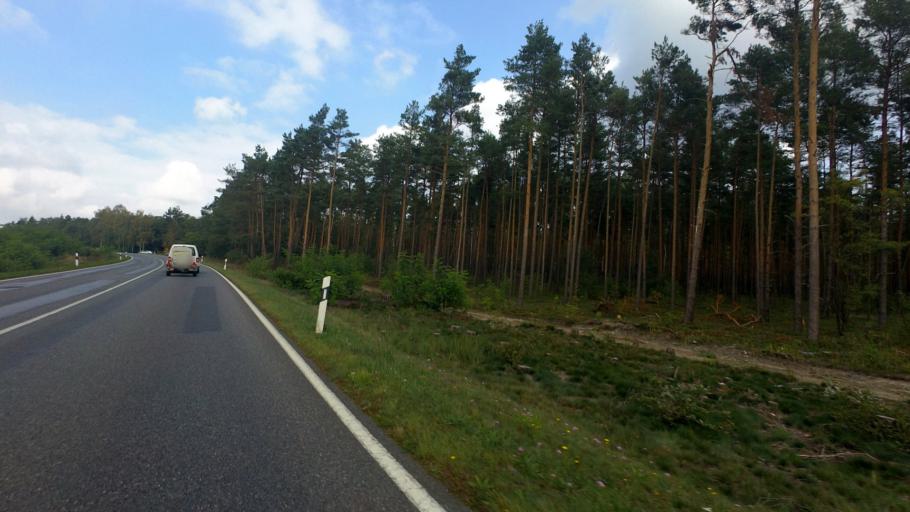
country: DE
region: Brandenburg
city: Elsterwerda
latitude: 51.5032
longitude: 13.4649
